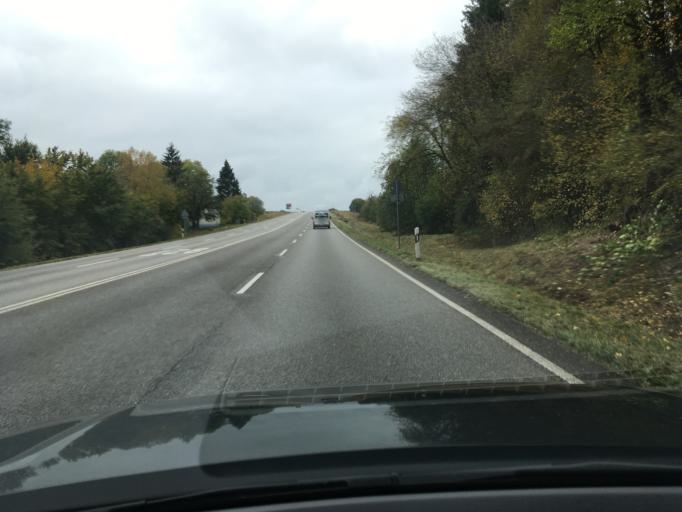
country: DE
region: Baden-Wuerttemberg
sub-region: Tuebingen Region
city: Ofterdingen
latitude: 48.4111
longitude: 9.0300
